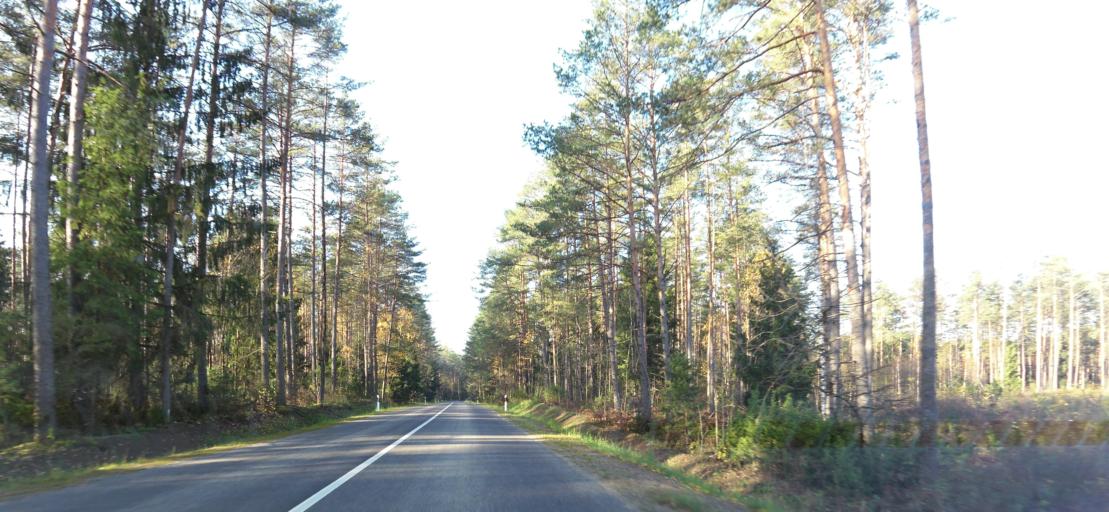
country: LT
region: Vilnius County
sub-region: Trakai
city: Rudiskes
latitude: 54.5102
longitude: 24.9100
